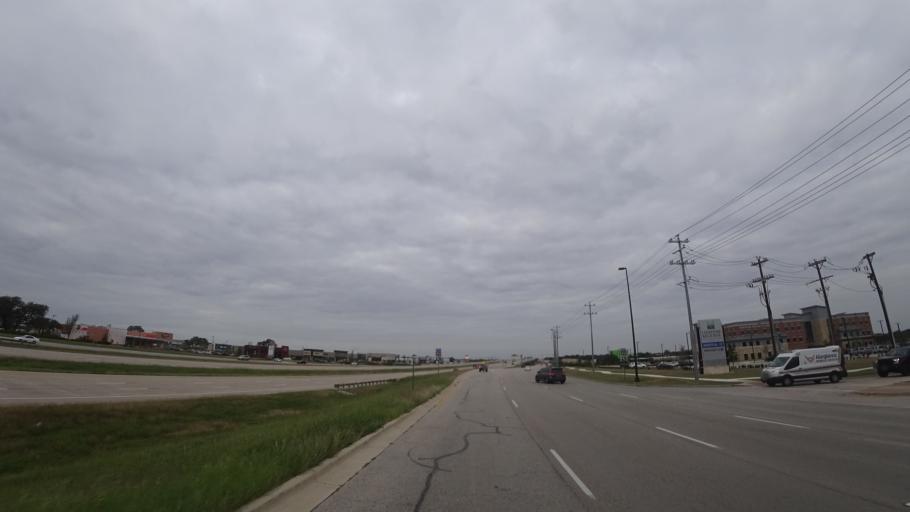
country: US
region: Texas
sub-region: Williamson County
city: Cedar Park
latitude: 30.5311
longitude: -97.8168
